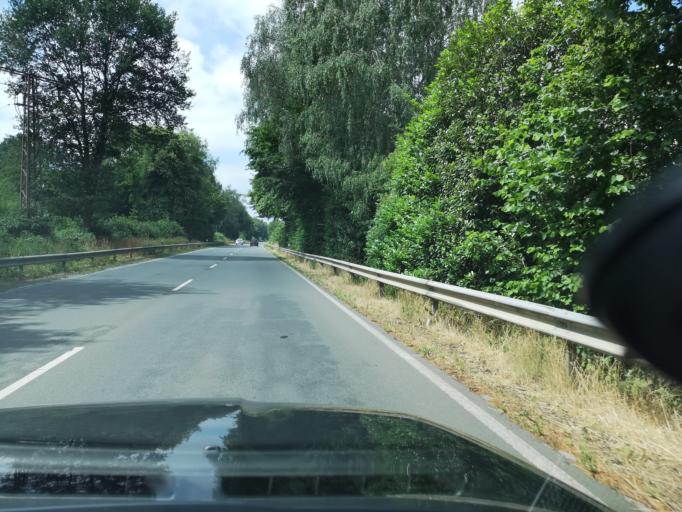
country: DE
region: North Rhine-Westphalia
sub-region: Regierungsbezirk Munster
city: Isselburg
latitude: 51.8561
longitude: 6.4847
